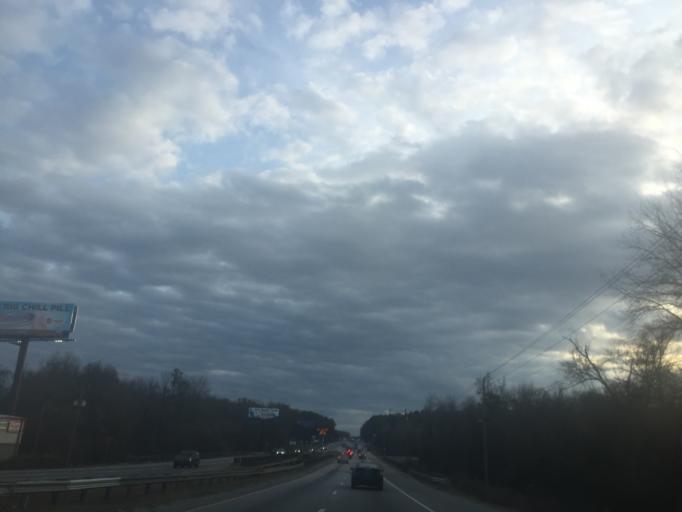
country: US
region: Georgia
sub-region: Clayton County
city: Riverdale
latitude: 33.6064
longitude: -84.4041
